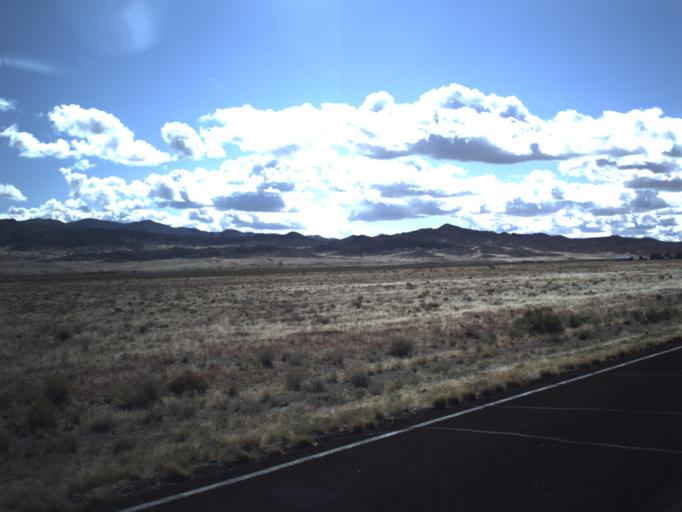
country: US
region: Nevada
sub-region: White Pine County
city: McGill
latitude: 38.9681
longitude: -114.0338
